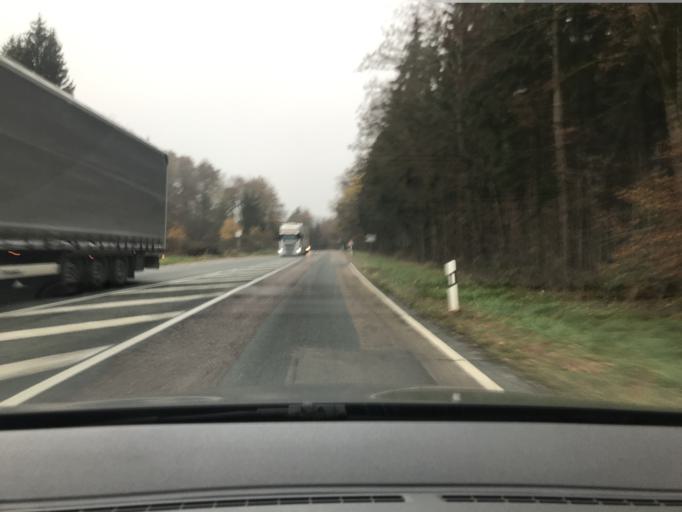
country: DE
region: Bavaria
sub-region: Swabia
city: Fremdingen
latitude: 48.9903
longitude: 10.4219
